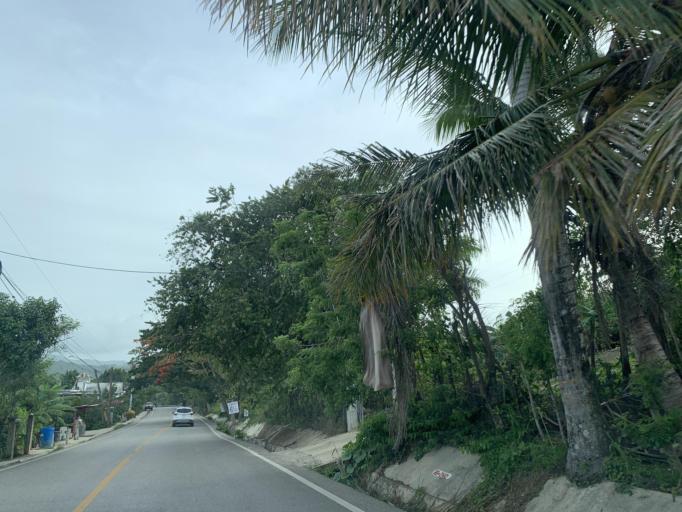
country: DO
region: Puerto Plata
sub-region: Puerto Plata
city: Puerto Plata
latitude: 19.7086
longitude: -70.6241
